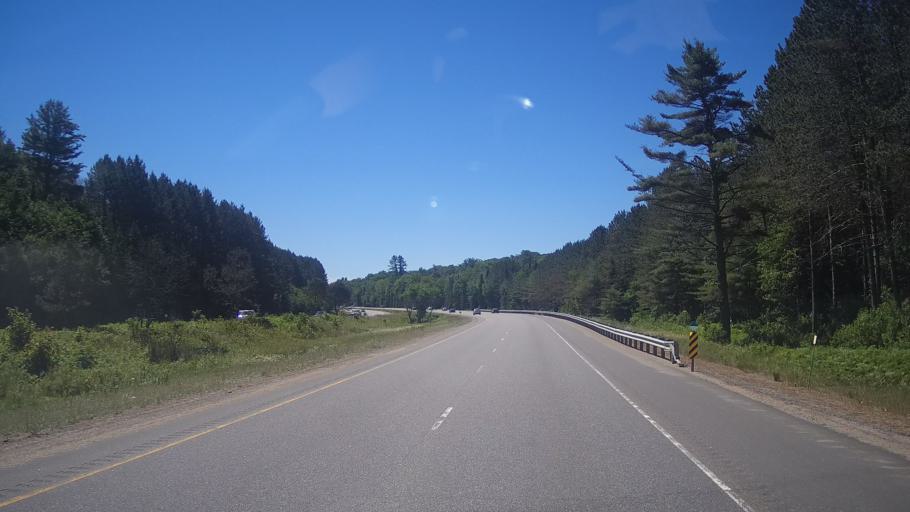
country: CA
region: Ontario
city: Bracebridge
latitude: 45.1077
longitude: -79.3109
